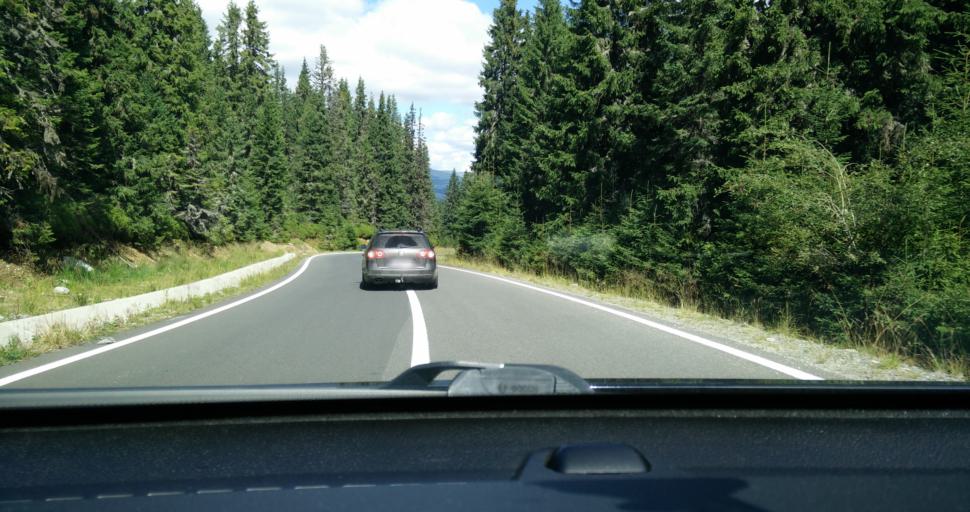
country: RO
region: Hunedoara
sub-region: Oras Petrila
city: Petrila
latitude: 45.4776
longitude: 23.6403
